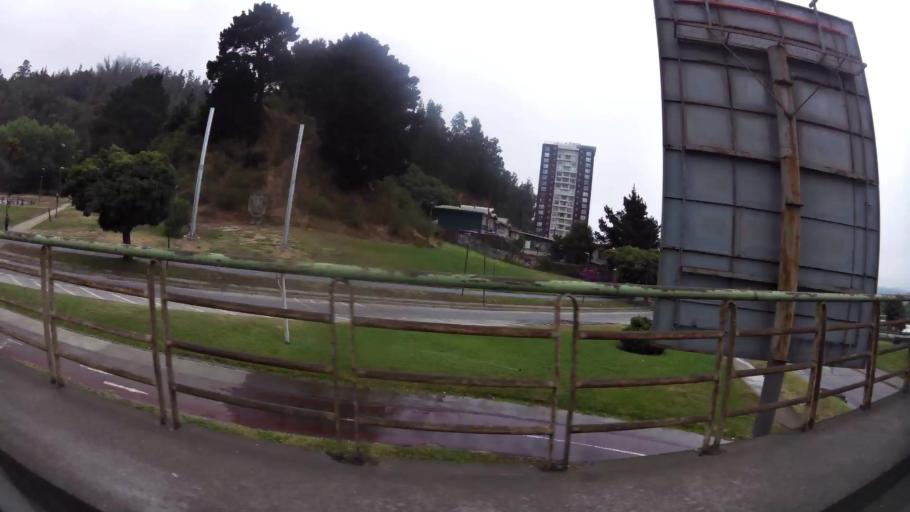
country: CL
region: Biobio
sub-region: Provincia de Concepcion
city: Concepcion
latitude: -36.8351
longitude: -73.0556
